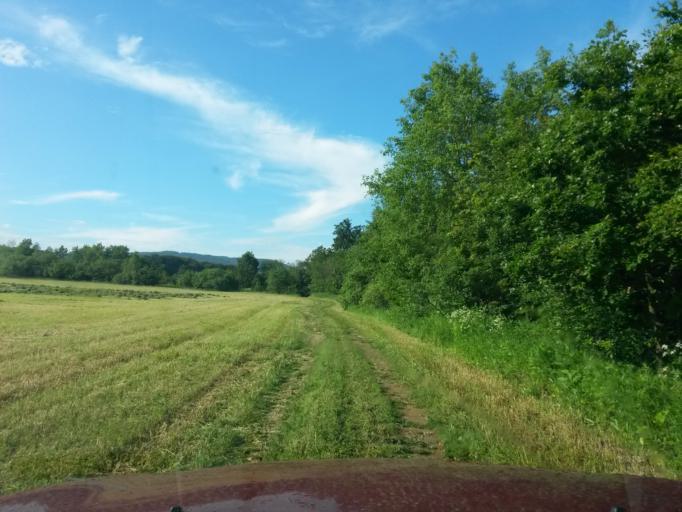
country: SK
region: Kosicky
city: Kosice
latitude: 48.7236
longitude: 21.1269
